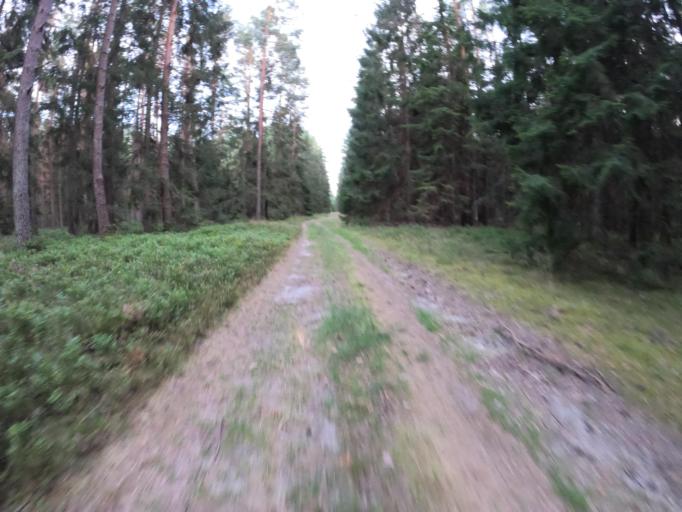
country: PL
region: West Pomeranian Voivodeship
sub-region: Powiat koszalinski
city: Sianow
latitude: 54.0918
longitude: 16.4087
